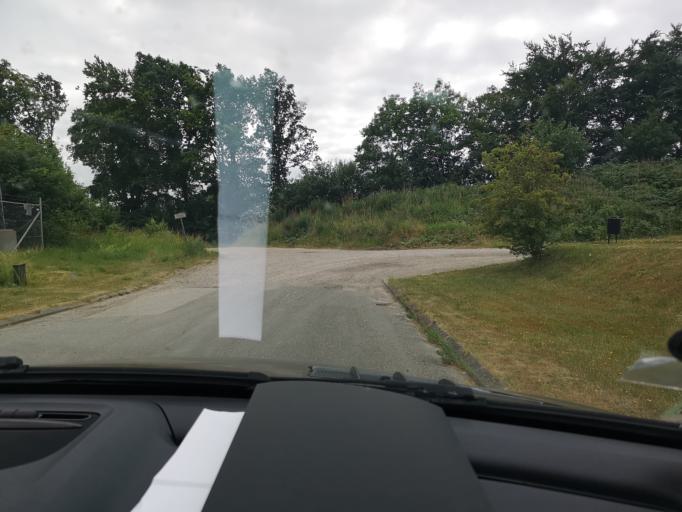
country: DK
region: Zealand
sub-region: Kalundborg Kommune
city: Kalundborg
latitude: 55.6772
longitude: 11.1207
